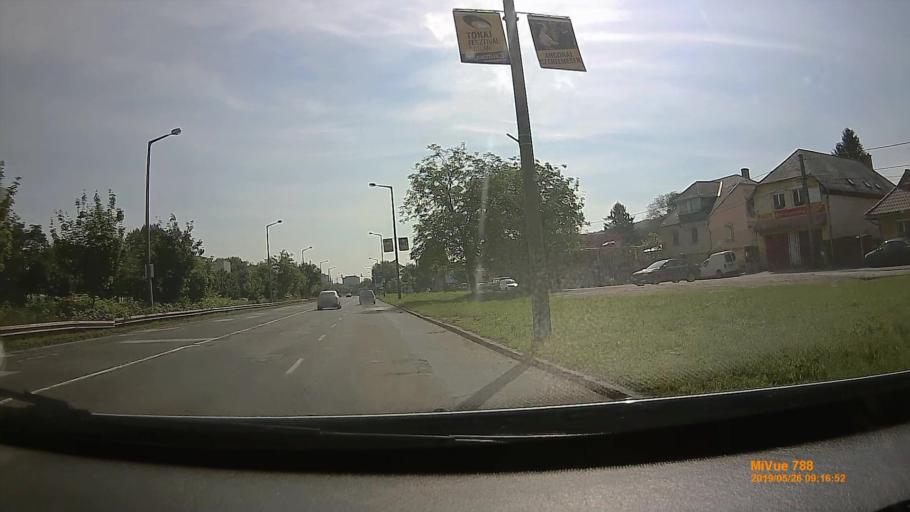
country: HU
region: Borsod-Abauj-Zemplen
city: Miskolc
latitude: 48.1001
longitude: 20.7565
